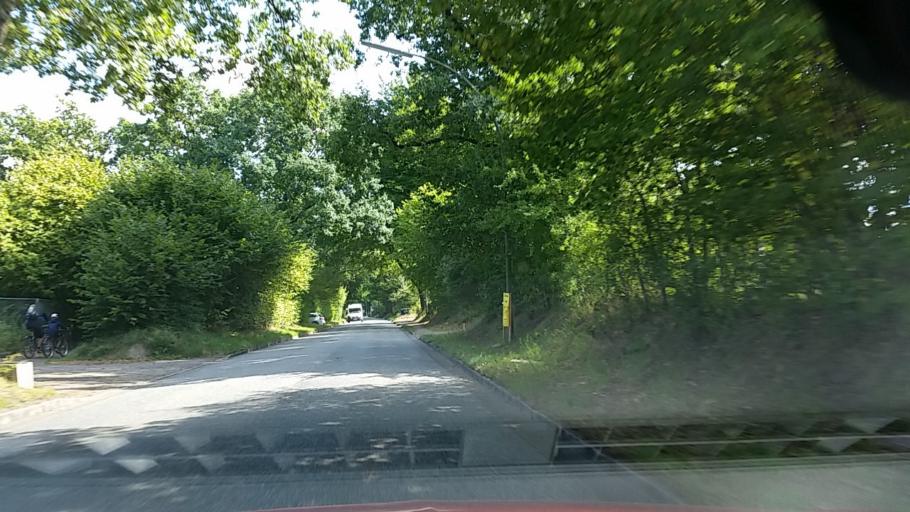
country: DE
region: Hamburg
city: Bergstedt
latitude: 53.6699
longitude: 10.1370
